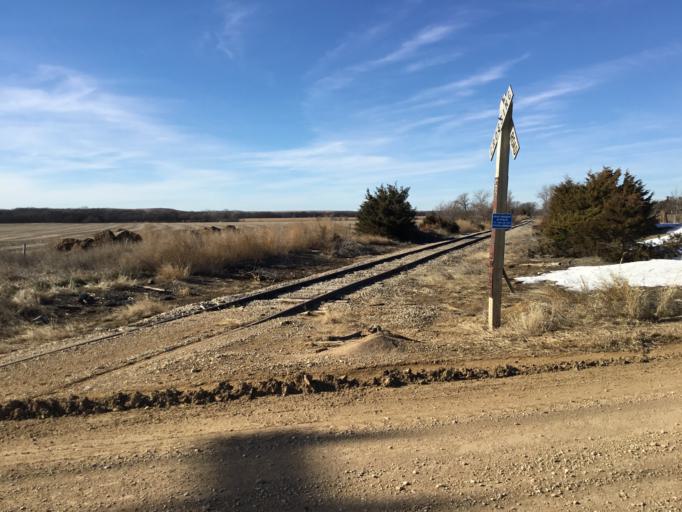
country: US
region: Kansas
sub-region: Lincoln County
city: Lincoln
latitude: 39.1051
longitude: -98.3164
